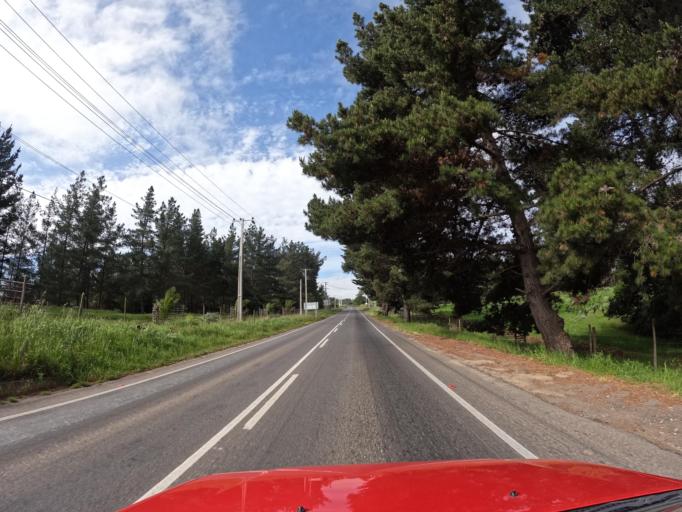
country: CL
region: O'Higgins
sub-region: Provincia de Colchagua
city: Santa Cruz
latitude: -34.3655
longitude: -71.9532
